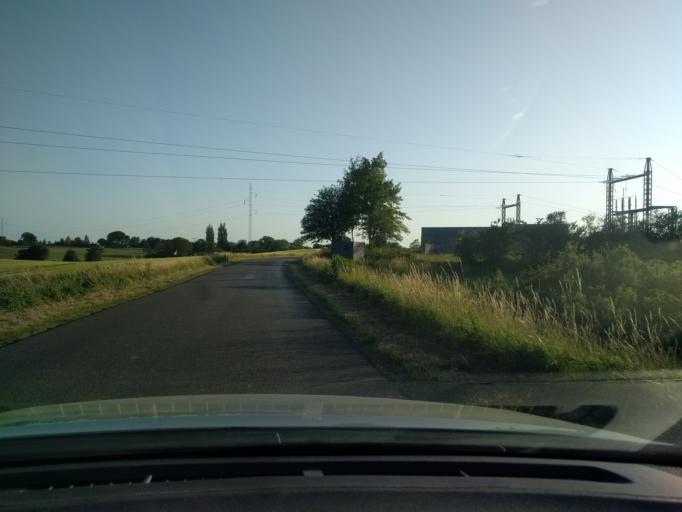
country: DK
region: Zealand
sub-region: Vordingborg Kommune
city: Stege
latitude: 54.9591
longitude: 12.2575
